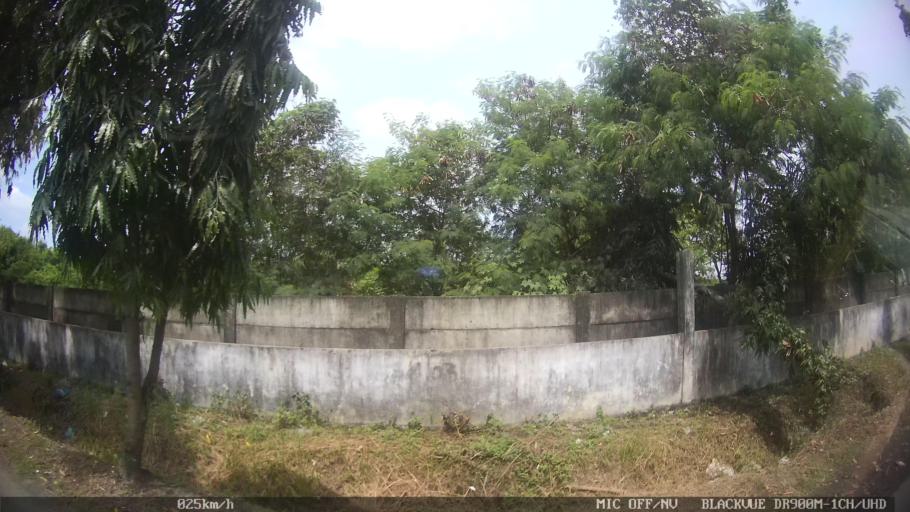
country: ID
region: North Sumatra
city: Medan
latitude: 3.6314
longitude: 98.7161
